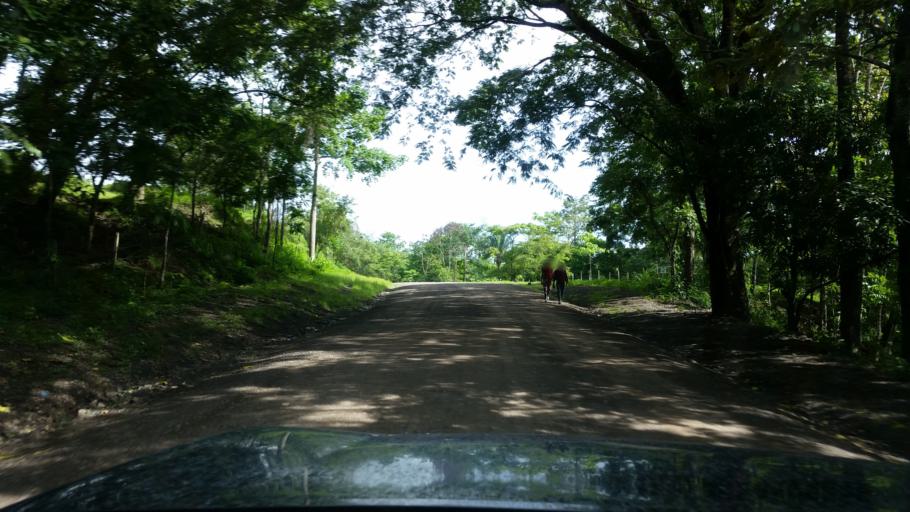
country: NI
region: Atlantico Norte (RAAN)
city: Siuna
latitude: 13.6575
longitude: -84.7937
